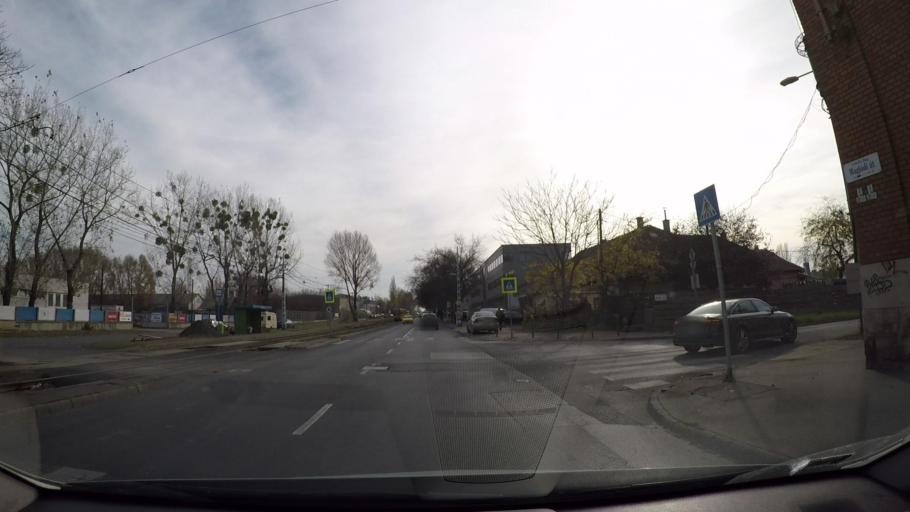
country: HU
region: Budapest
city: Budapest X. keruelet
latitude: 47.4829
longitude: 19.1582
